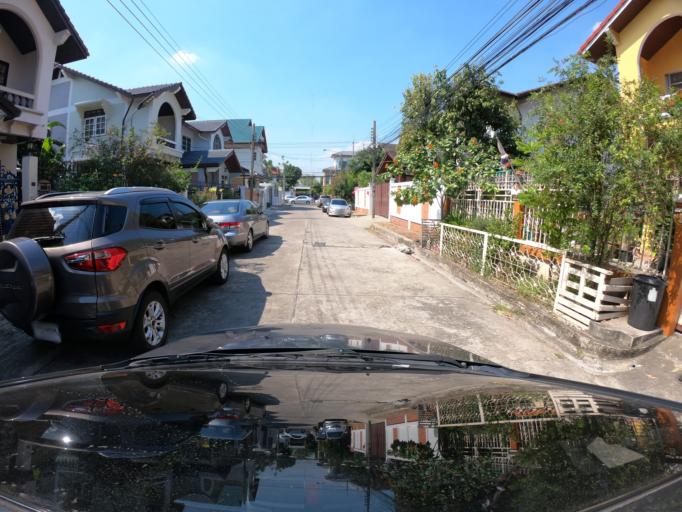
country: TH
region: Bangkok
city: Bang Na
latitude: 13.6664
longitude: 100.6141
